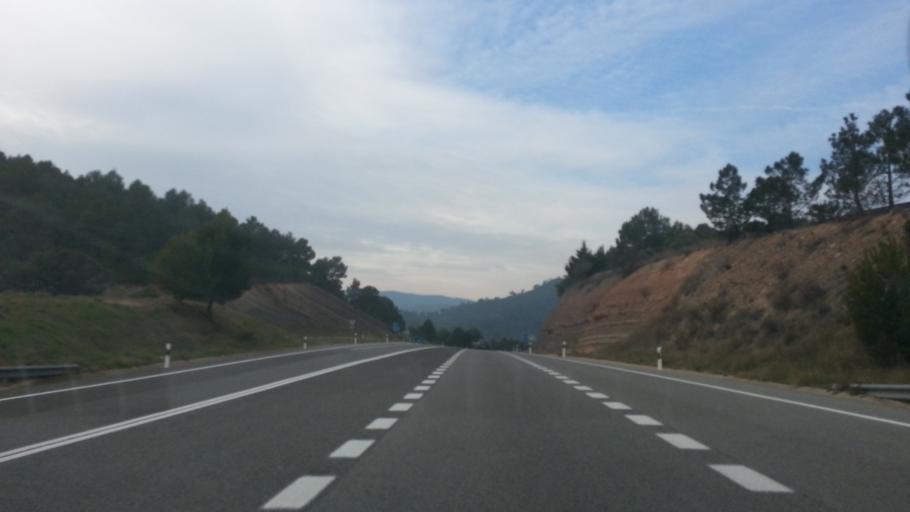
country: ES
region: Catalonia
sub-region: Provincia de Barcelona
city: Suria
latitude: 41.8397
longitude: 1.7367
